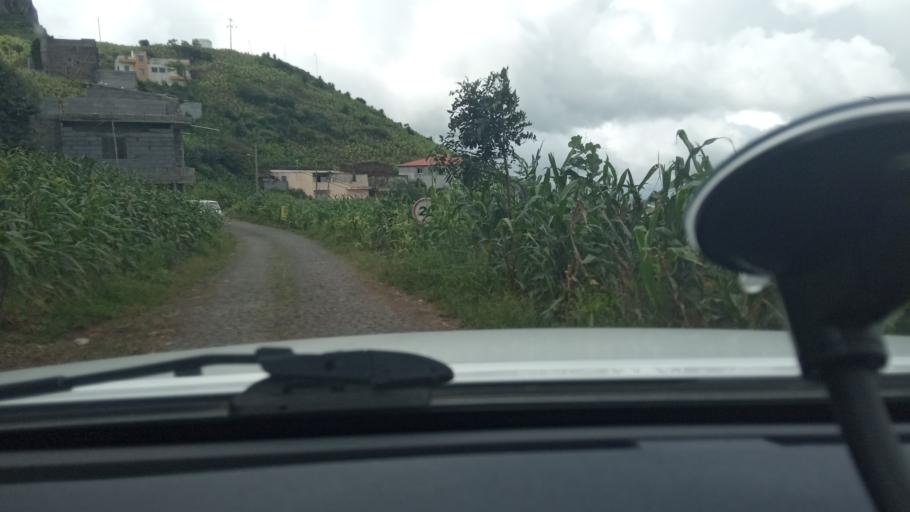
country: CV
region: Sao Salvador do Mundo
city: Picos
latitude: 15.0878
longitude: -23.6506
